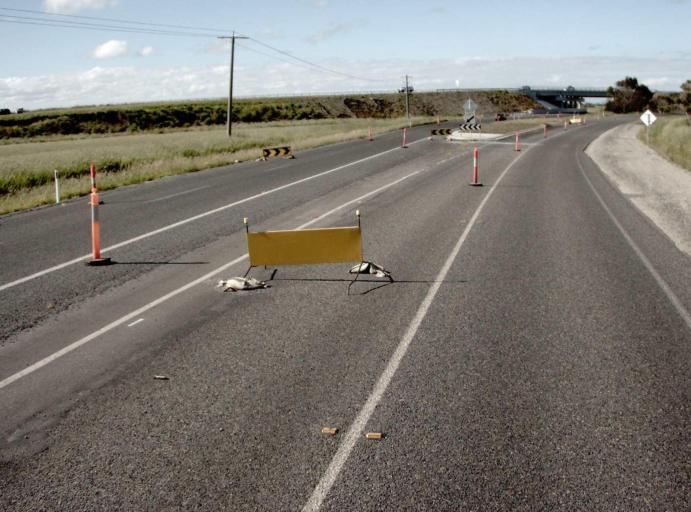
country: AU
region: Victoria
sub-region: Bass Coast
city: North Wonthaggi
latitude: -38.5101
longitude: 145.4501
